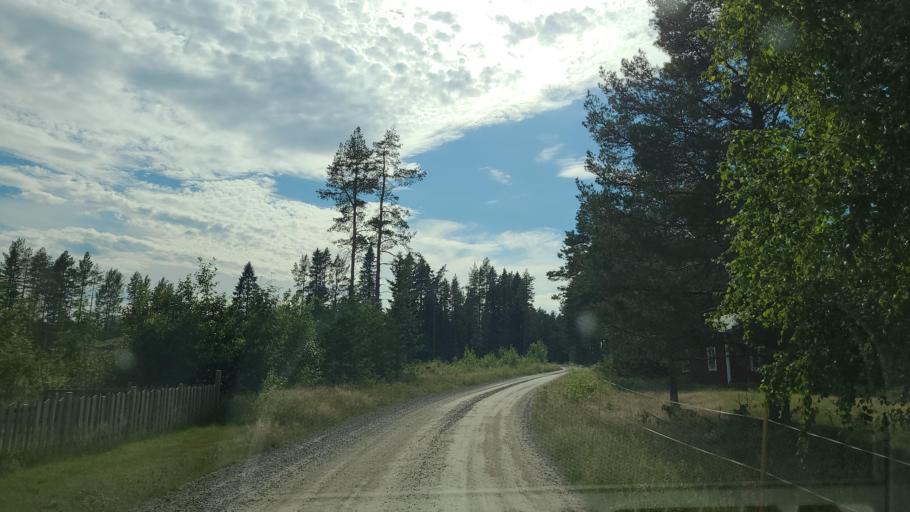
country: SE
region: Vaesterbotten
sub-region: Robertsfors Kommun
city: Robertsfors
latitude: 64.1571
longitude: 20.9322
